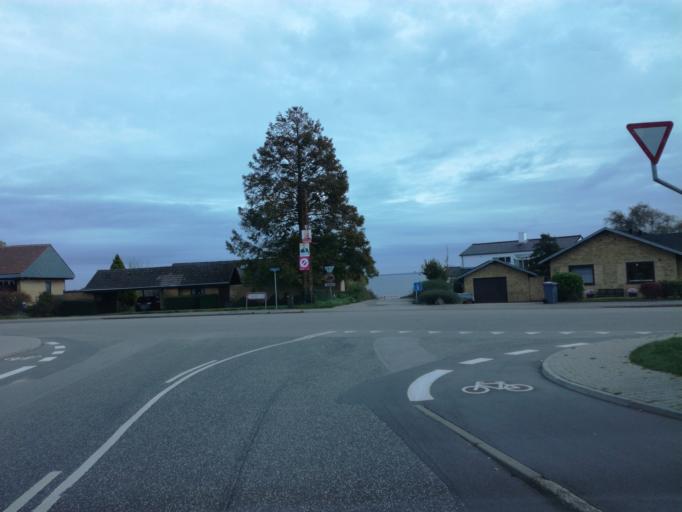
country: DK
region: South Denmark
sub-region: Fredericia Kommune
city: Fredericia
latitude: 55.5782
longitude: 9.7795
